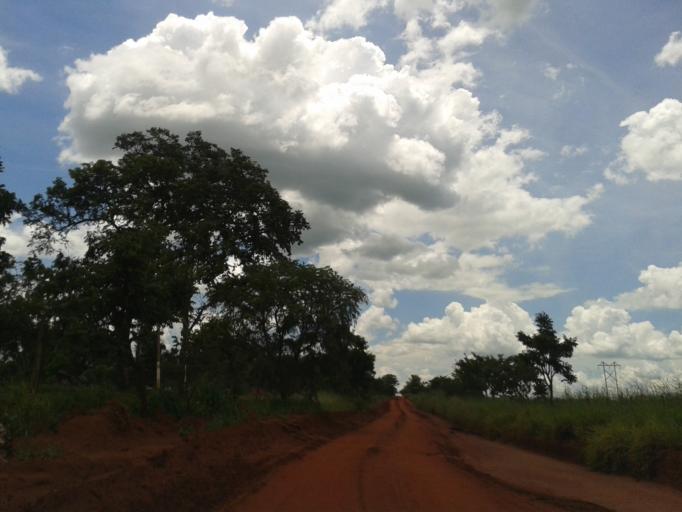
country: BR
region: Minas Gerais
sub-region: Ituiutaba
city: Ituiutaba
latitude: -18.9014
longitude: -49.4561
